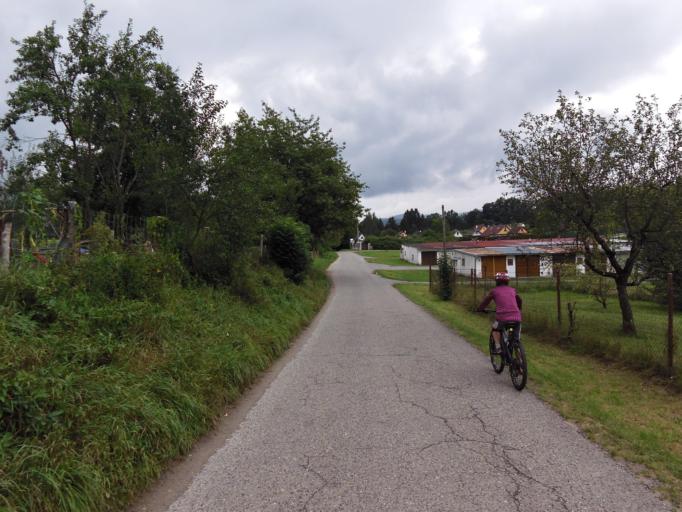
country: CZ
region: Jihocesky
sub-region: Okres Ceske Budejovice
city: Nove Hrady
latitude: 48.7860
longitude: 14.7840
